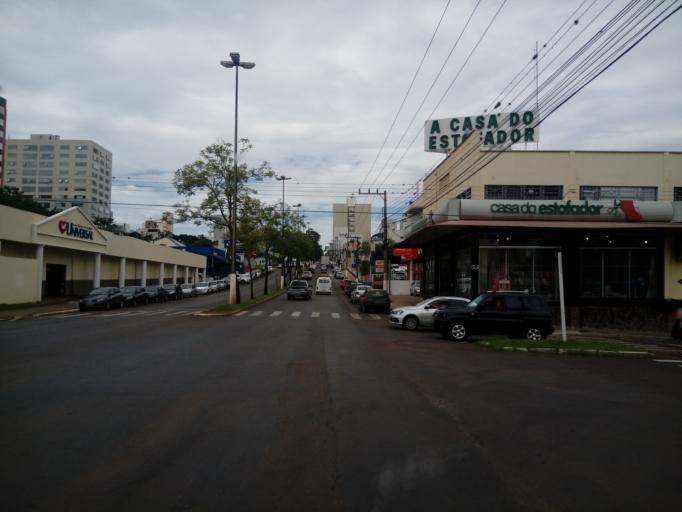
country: BR
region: Santa Catarina
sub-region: Chapeco
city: Chapeco
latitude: -27.1001
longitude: -52.6208
